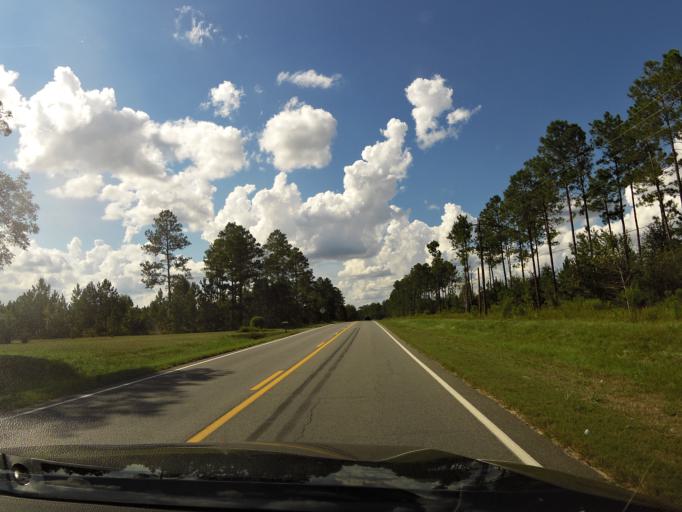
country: US
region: Georgia
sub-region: Lowndes County
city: Valdosta
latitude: 30.8026
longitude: -83.2013
